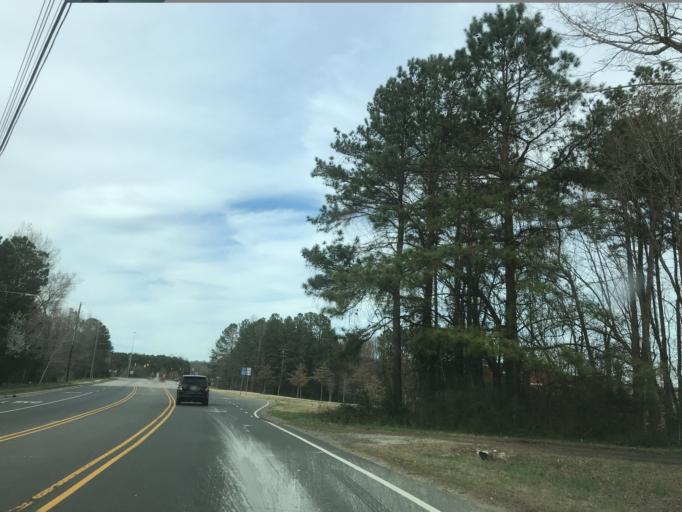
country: US
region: North Carolina
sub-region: Wake County
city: West Raleigh
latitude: 35.7538
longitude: -78.6667
